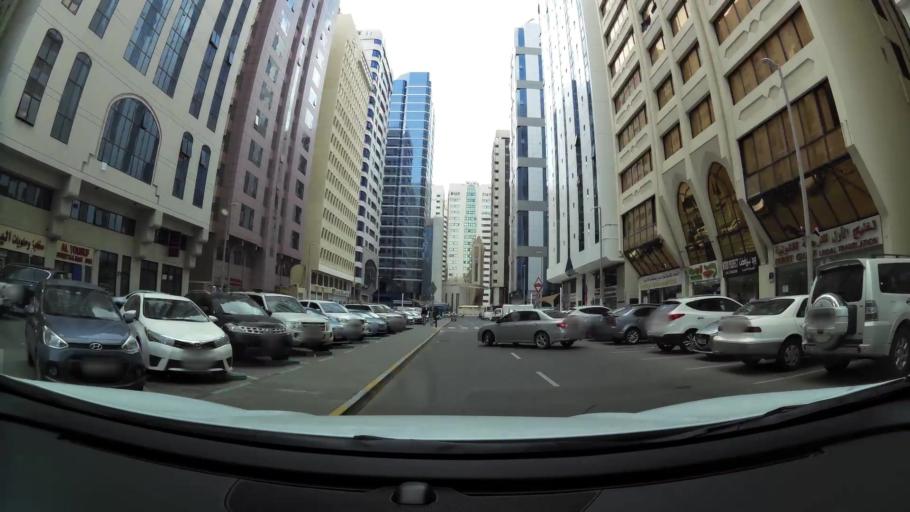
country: AE
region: Abu Dhabi
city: Abu Dhabi
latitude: 24.4899
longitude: 54.3617
